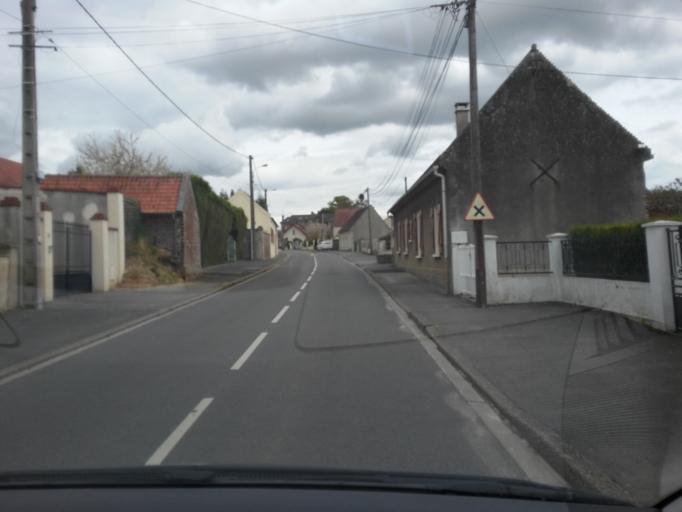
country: FR
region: Picardie
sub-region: Departement de l'Oise
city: Grandfresnoy
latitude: 49.3666
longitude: 2.6527
